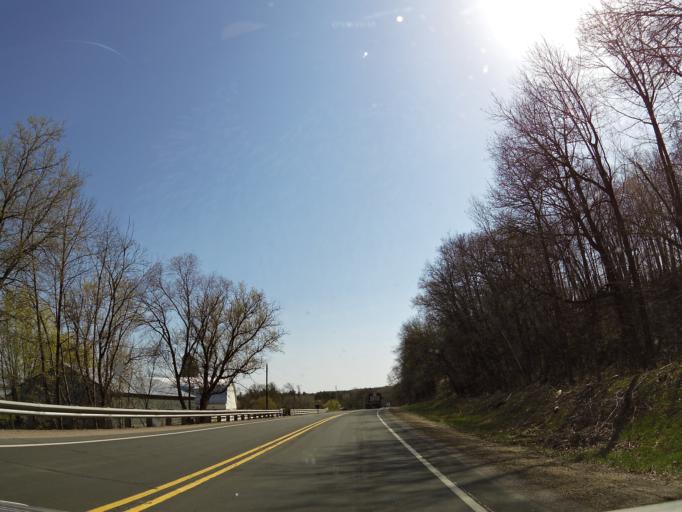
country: US
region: Wisconsin
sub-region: Pepin County
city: Durand
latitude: 44.7484
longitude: -91.9301
